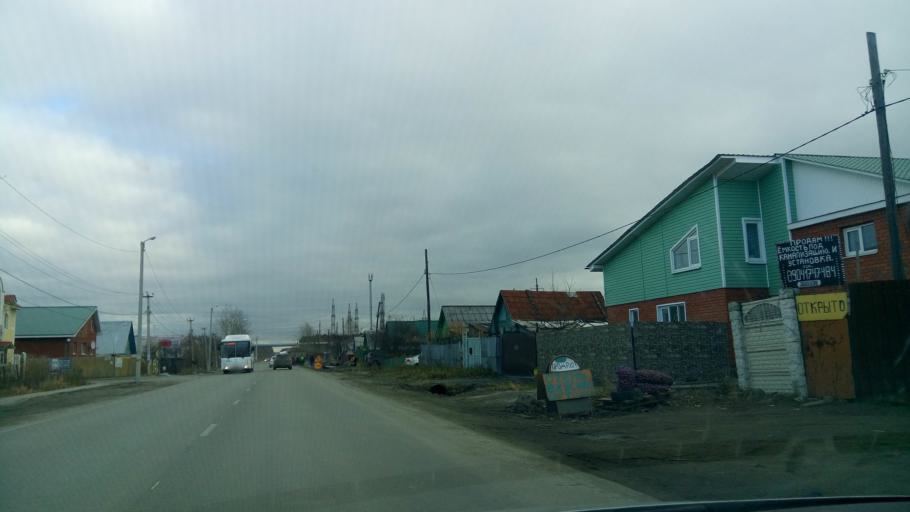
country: RU
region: Sverdlovsk
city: Sredneuralsk
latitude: 56.9898
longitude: 60.4911
